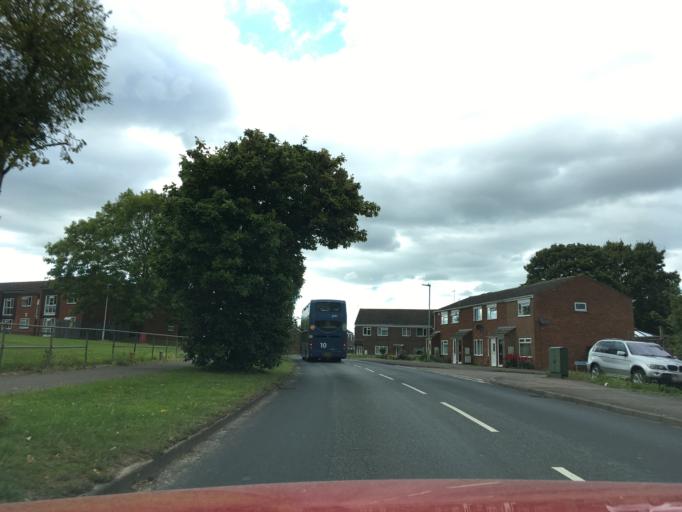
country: GB
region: England
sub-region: Gloucestershire
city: Gloucester
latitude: 51.8427
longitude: -2.2278
